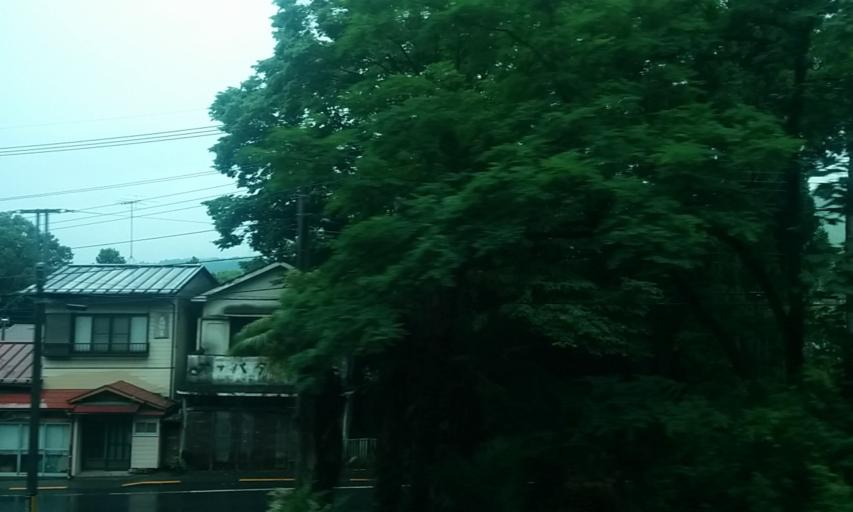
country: JP
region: Tokyo
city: Ome
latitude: 35.7894
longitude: 139.2404
